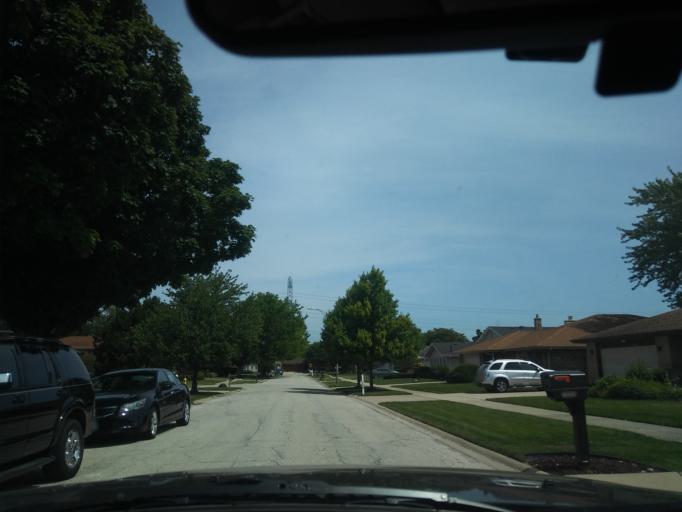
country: US
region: Illinois
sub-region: Cook County
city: Tinley Park
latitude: 41.6077
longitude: -87.8044
